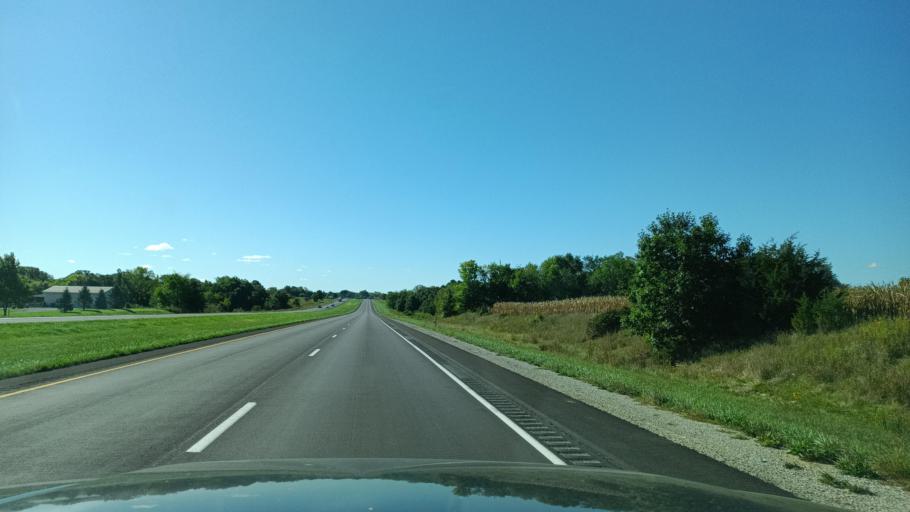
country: US
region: Iowa
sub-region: Lee County
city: Keokuk
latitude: 40.4580
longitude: -91.4437
